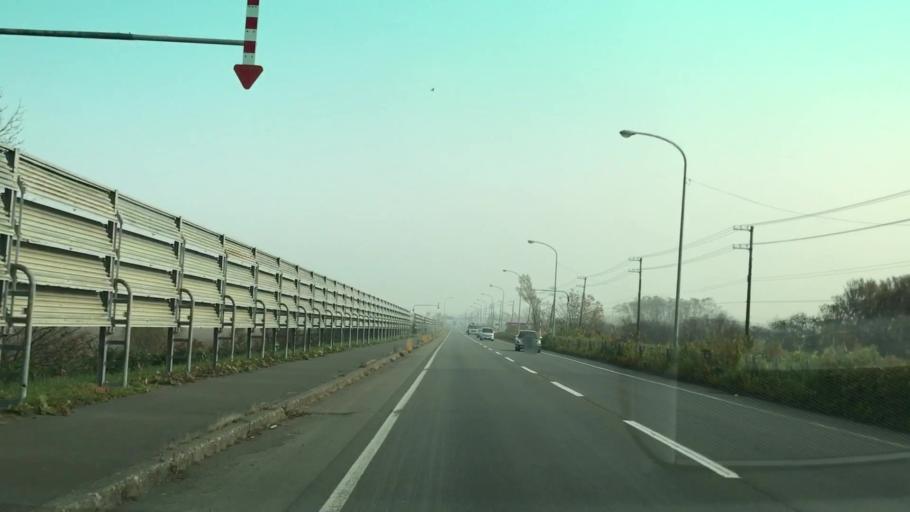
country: JP
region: Hokkaido
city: Ishikari
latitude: 43.2386
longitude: 141.3643
